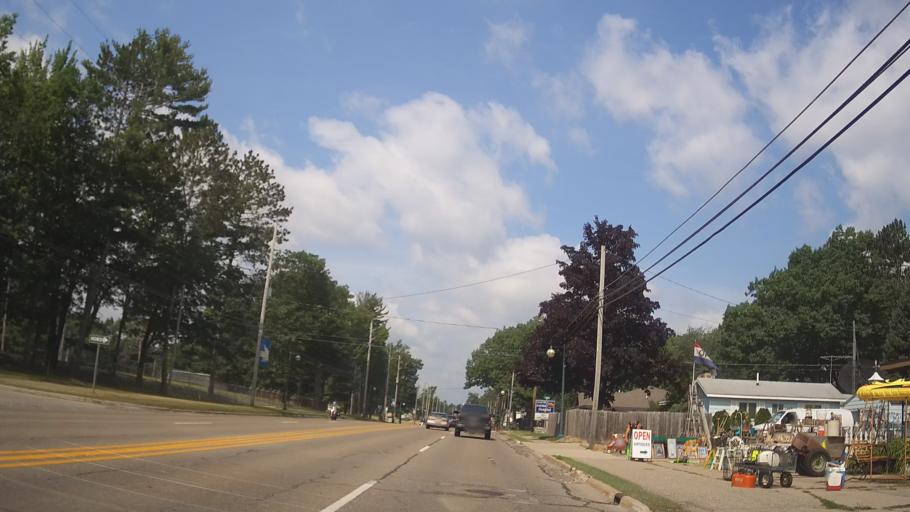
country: US
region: Michigan
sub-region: Roscommon County
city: Houghton Lake
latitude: 44.2984
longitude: -84.7231
